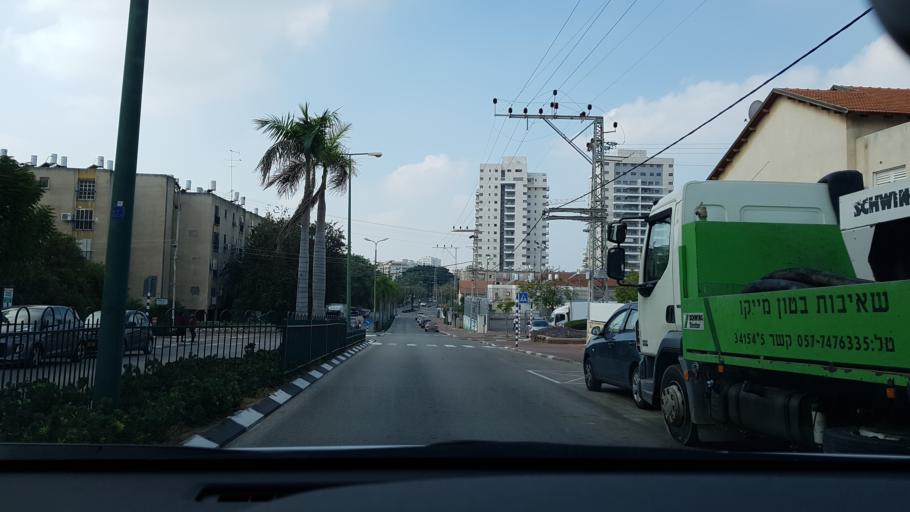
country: IL
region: Central District
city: Mazkeret Batya
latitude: 31.8842
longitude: 34.8232
